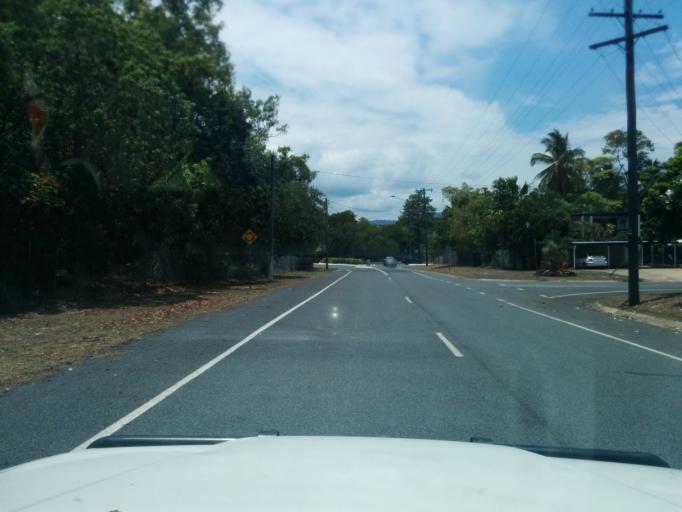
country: AU
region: Queensland
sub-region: Cairns
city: Yorkeys Knob
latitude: -16.8421
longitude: 145.7366
